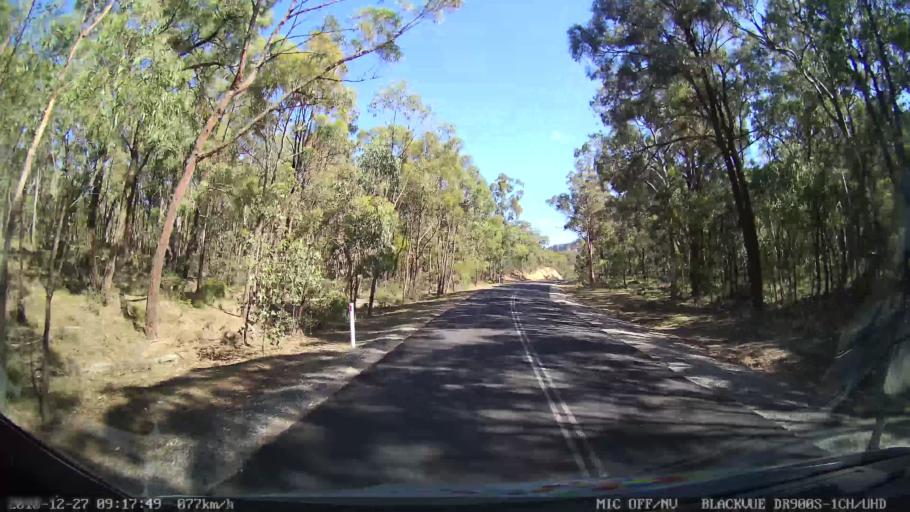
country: AU
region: New South Wales
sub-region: Lithgow
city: Portland
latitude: -33.1337
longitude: 150.0463
